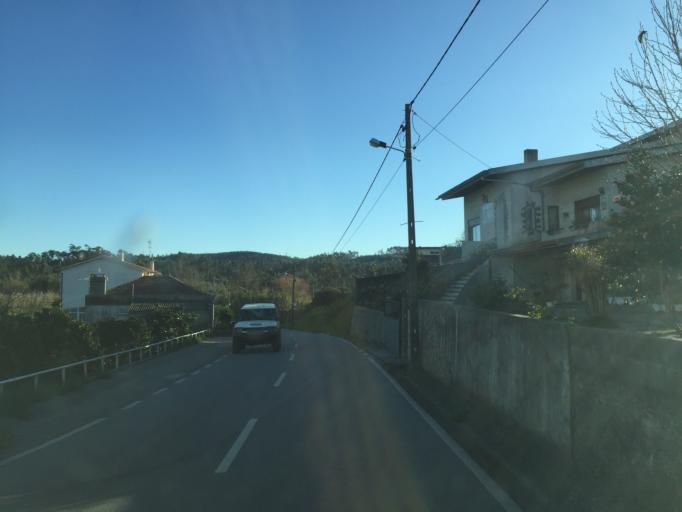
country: PT
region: Coimbra
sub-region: Figueira da Foz
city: Tavarede
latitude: 40.1634
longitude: -8.8179
